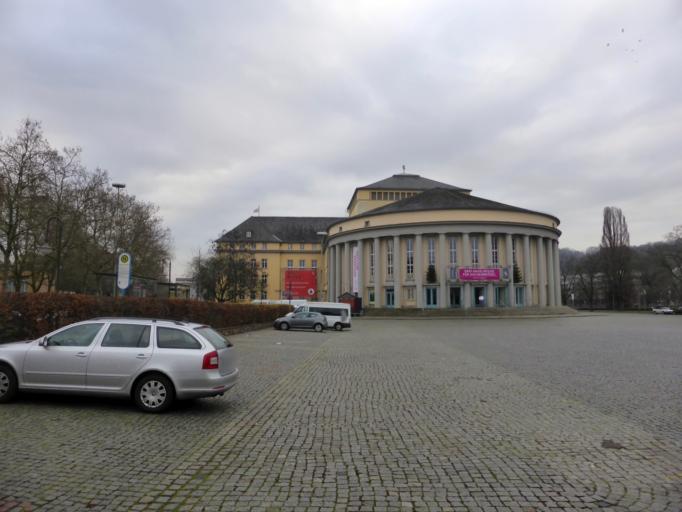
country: DE
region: Saarland
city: Saarbrucken
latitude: 49.2296
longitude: 6.9896
